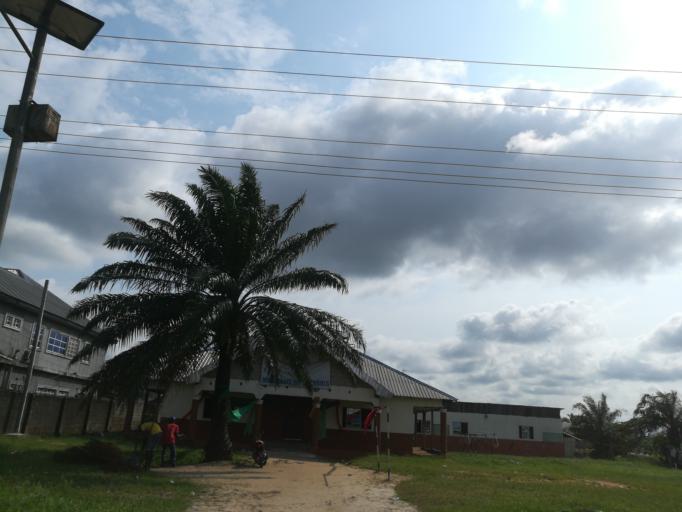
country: NG
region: Rivers
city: Okrika
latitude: 4.7599
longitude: 7.0844
